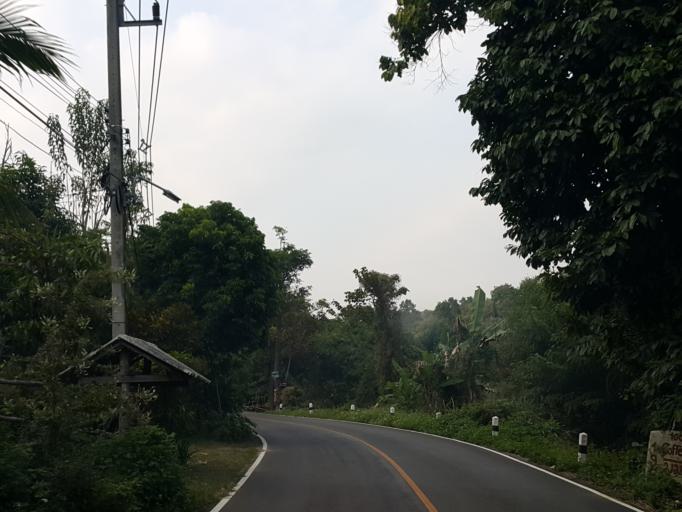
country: TH
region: Chiang Mai
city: Mae On
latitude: 18.9071
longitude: 99.2516
